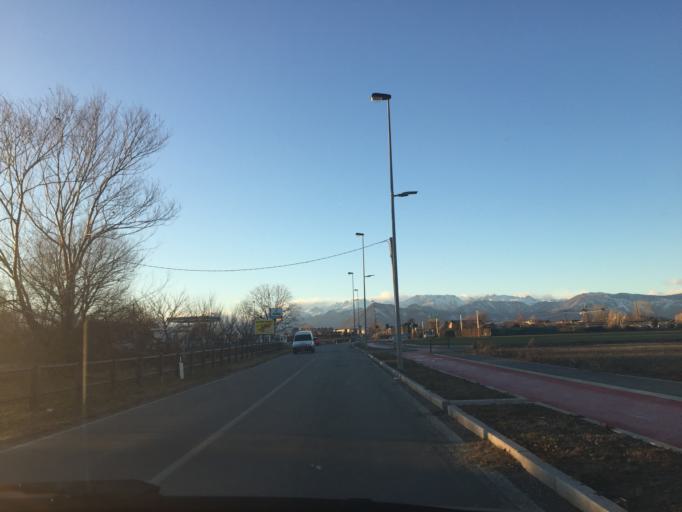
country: IT
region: Piedmont
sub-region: Provincia di Torino
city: Grugliasco
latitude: 45.0533
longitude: 7.5981
